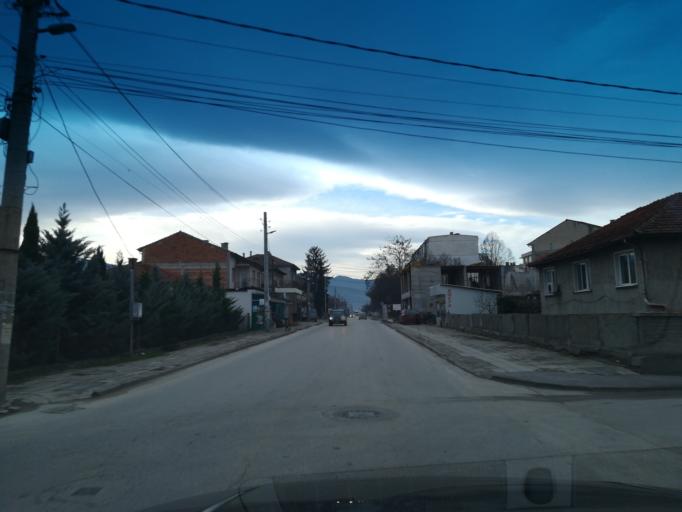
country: BG
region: Plovdiv
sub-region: Obshtina Plovdiv
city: Plovdiv
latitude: 42.0997
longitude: 24.7014
